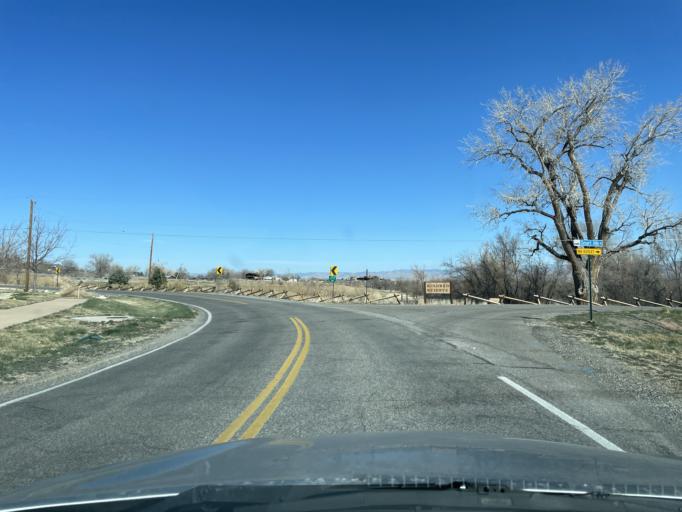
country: US
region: Colorado
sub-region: Mesa County
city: Redlands
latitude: 39.0773
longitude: -108.6640
